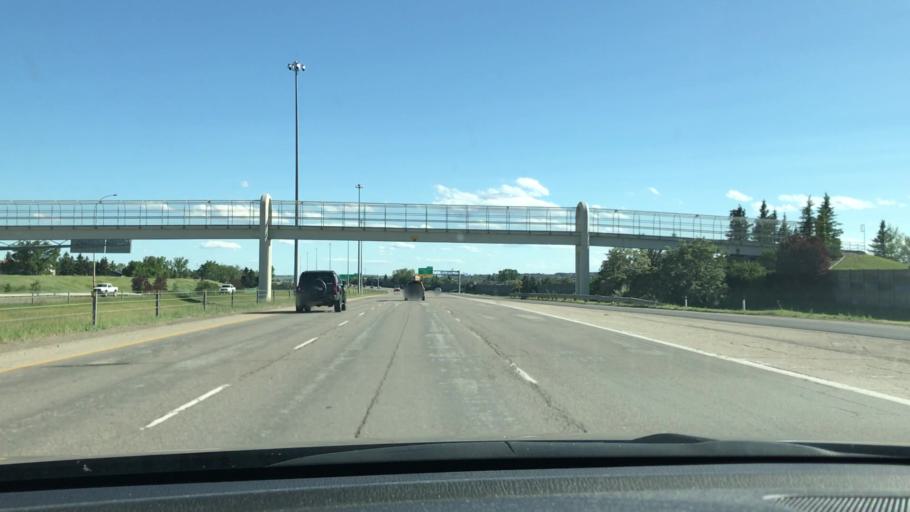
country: CA
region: Alberta
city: Airdrie
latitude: 51.2839
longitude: -114.0016
